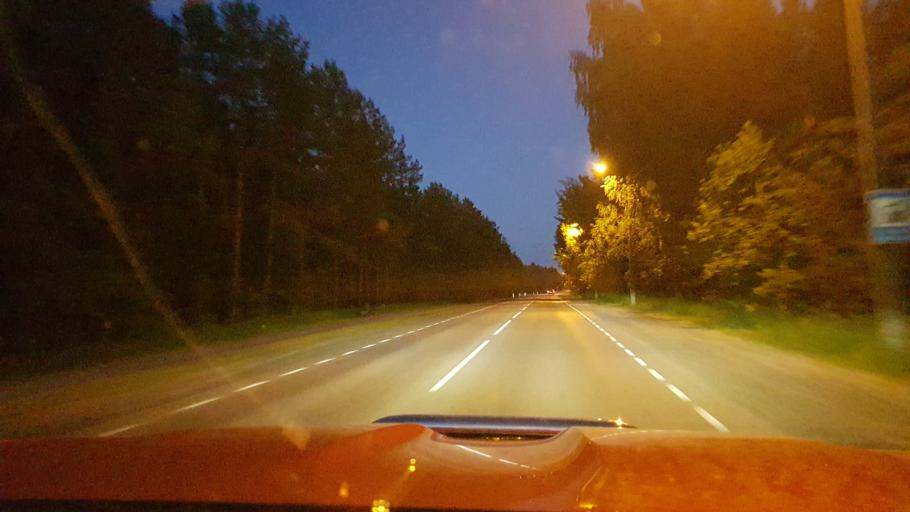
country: EE
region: Harju
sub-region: Tallinna linn
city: Tallinn
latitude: 59.3748
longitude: 24.7484
